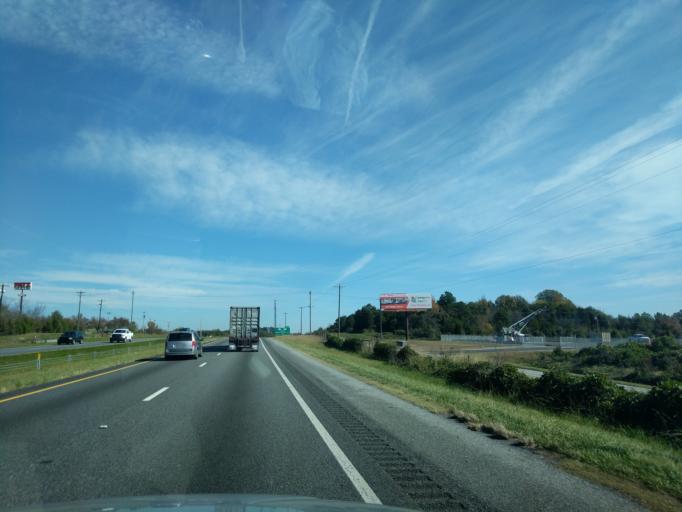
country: US
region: South Carolina
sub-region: Cherokee County
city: Gaffney
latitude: 35.0921
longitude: -81.6886
